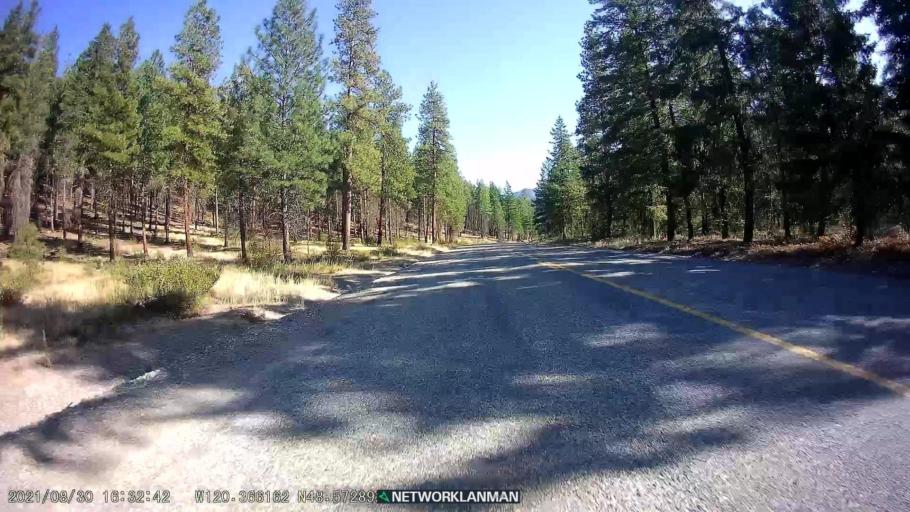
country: US
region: Washington
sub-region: Chelan County
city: Granite Falls
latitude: 48.5731
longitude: -120.3664
